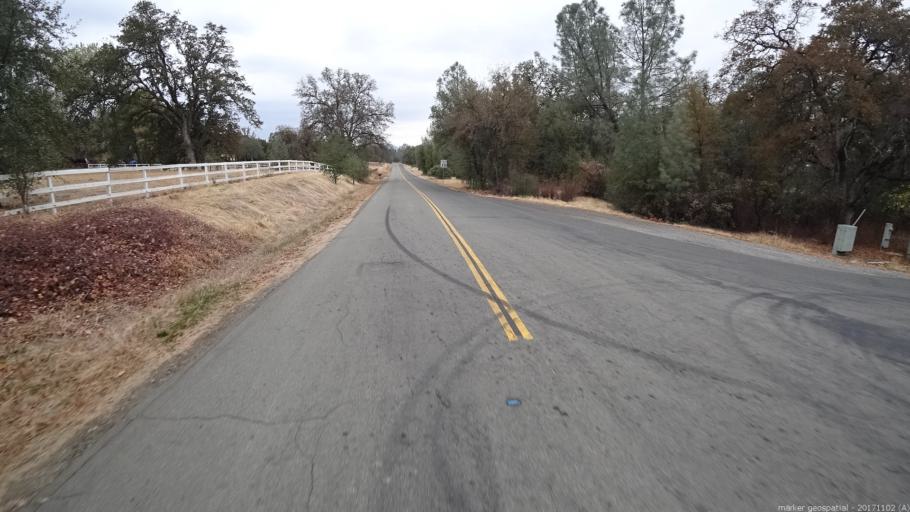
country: US
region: California
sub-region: Shasta County
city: Shasta Lake
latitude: 40.6531
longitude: -122.3167
